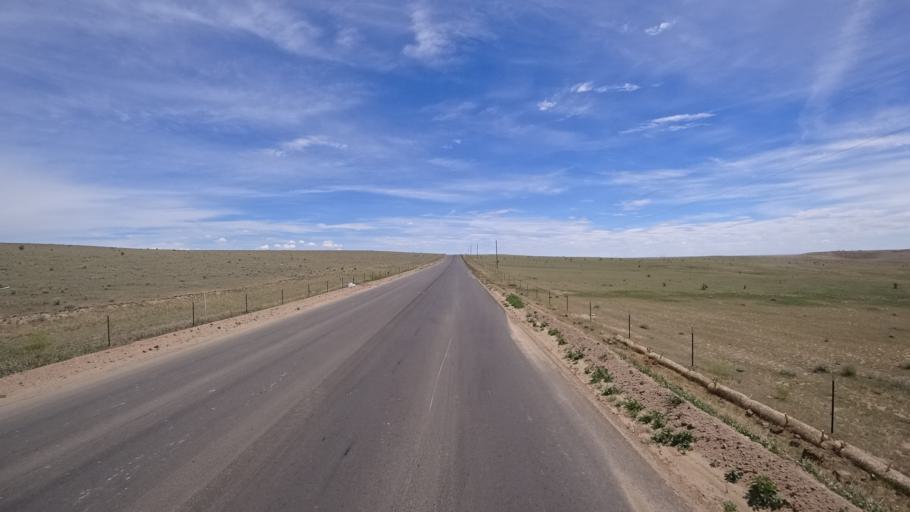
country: US
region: Colorado
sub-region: El Paso County
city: Fountain
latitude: 38.6940
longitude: -104.6473
